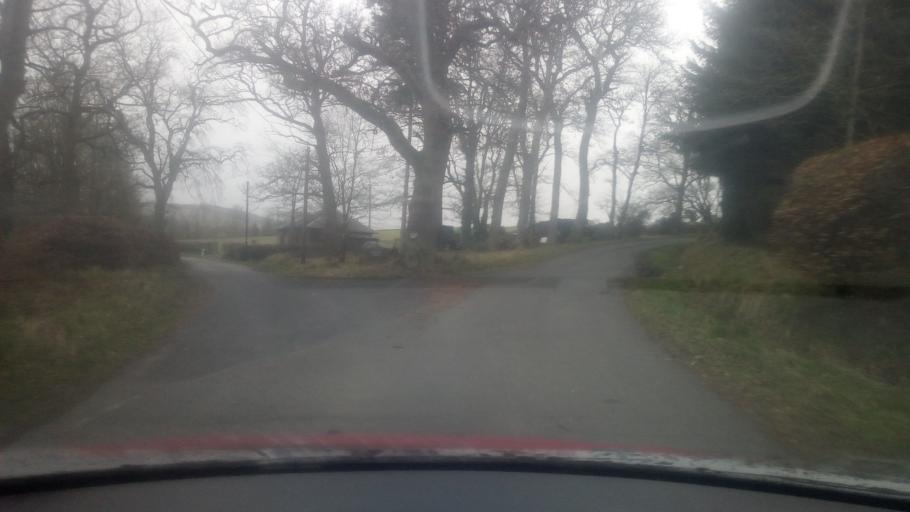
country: GB
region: Scotland
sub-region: The Scottish Borders
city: Hawick
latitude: 55.3811
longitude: -2.6600
